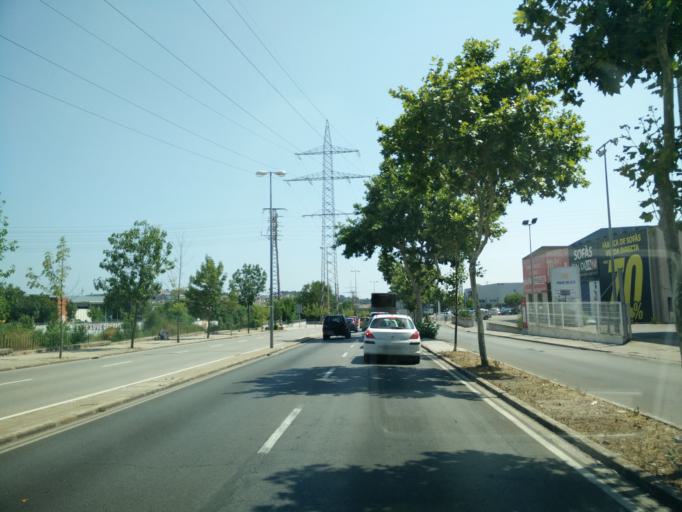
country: ES
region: Catalonia
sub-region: Provincia de Barcelona
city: Terrassa
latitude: 41.5490
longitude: 2.0391
